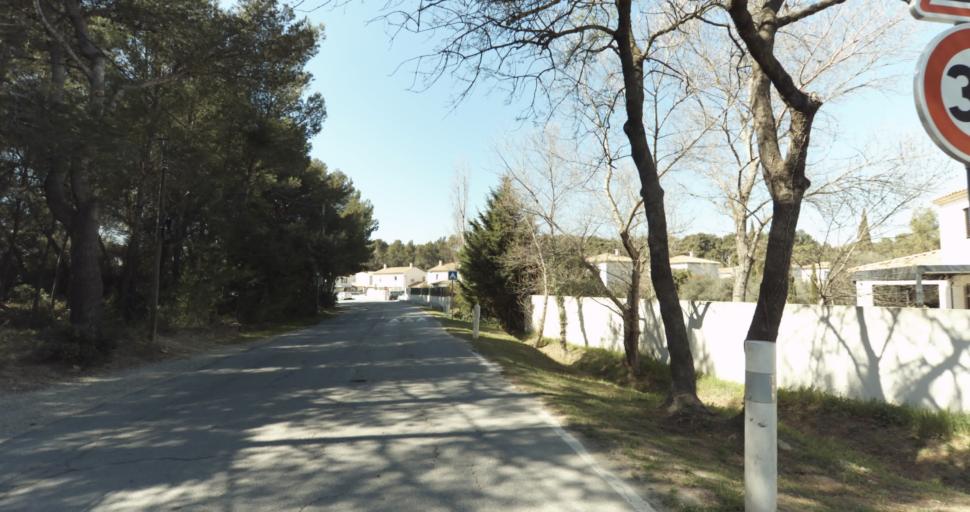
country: FR
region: Provence-Alpes-Cote d'Azur
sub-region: Departement des Bouches-du-Rhone
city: Pelissanne
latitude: 43.6346
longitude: 5.1652
